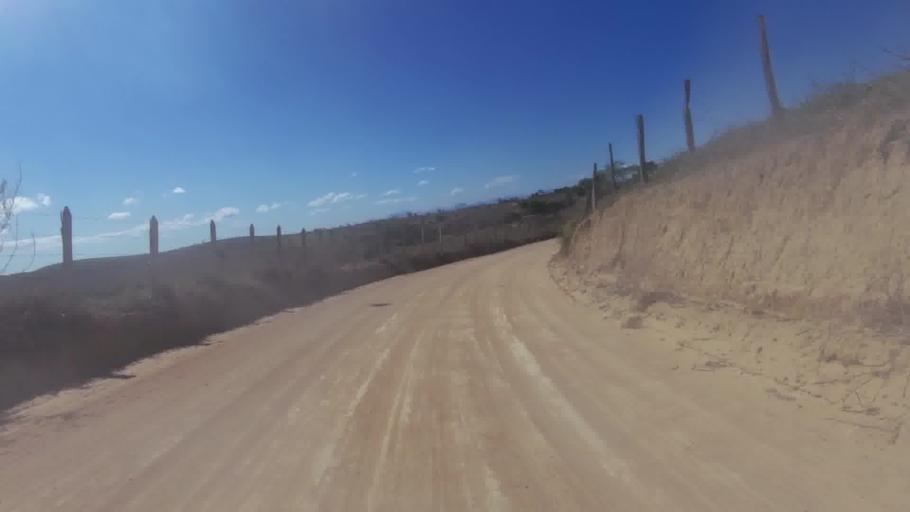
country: BR
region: Espirito Santo
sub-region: Marataizes
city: Marataizes
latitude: -21.1538
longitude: -40.9830
